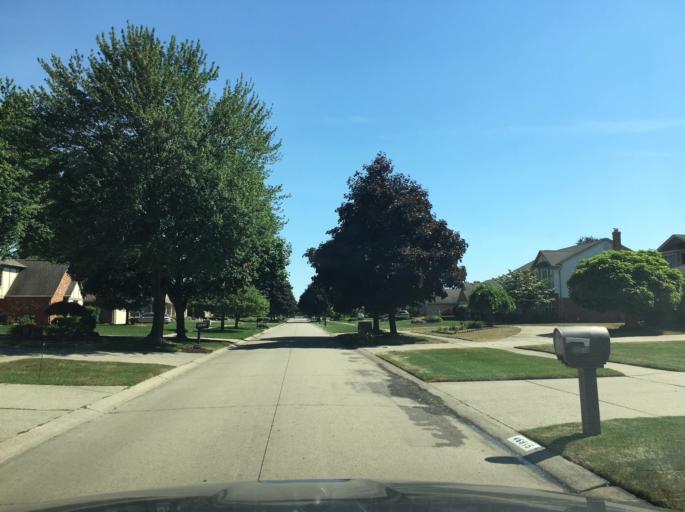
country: US
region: Michigan
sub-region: Macomb County
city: Utica
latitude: 42.6398
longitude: -83.0083
